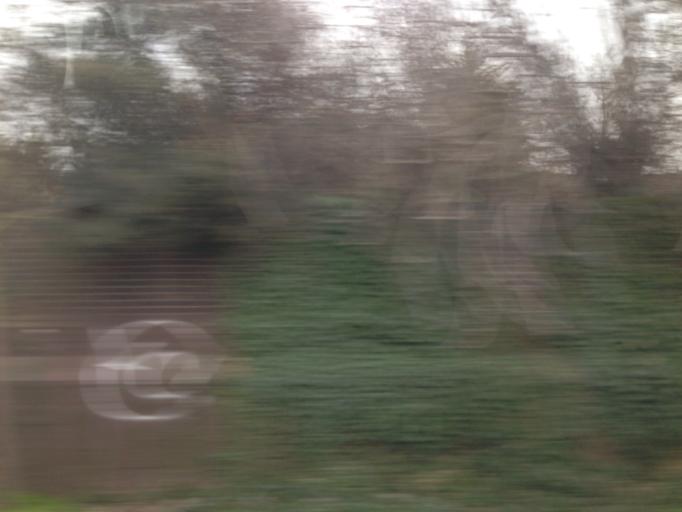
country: GB
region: England
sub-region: Greater London
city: Brixton Hill
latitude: 51.4250
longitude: -0.1387
